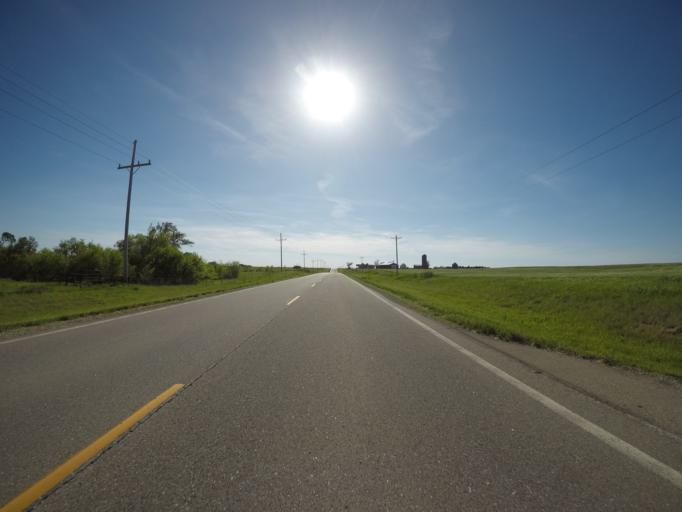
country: US
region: Kansas
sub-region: Clay County
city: Clay Center
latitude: 39.3647
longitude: -96.8990
